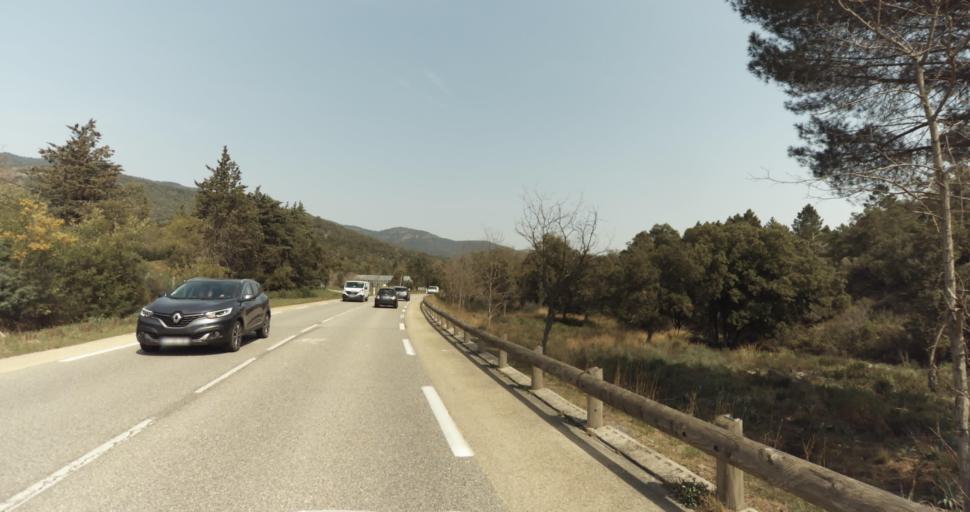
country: FR
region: Provence-Alpes-Cote d'Azur
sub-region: Departement du Var
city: Le Lavandou
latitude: 43.1936
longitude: 6.3783
